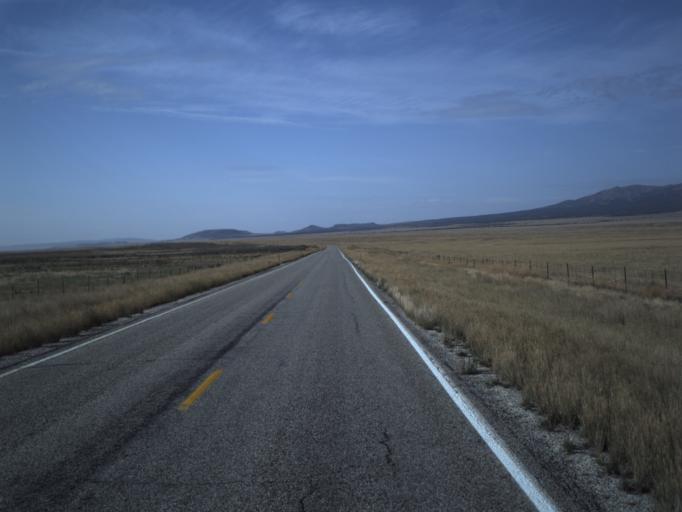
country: US
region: Idaho
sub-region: Oneida County
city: Malad City
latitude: 41.9551
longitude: -113.0724
